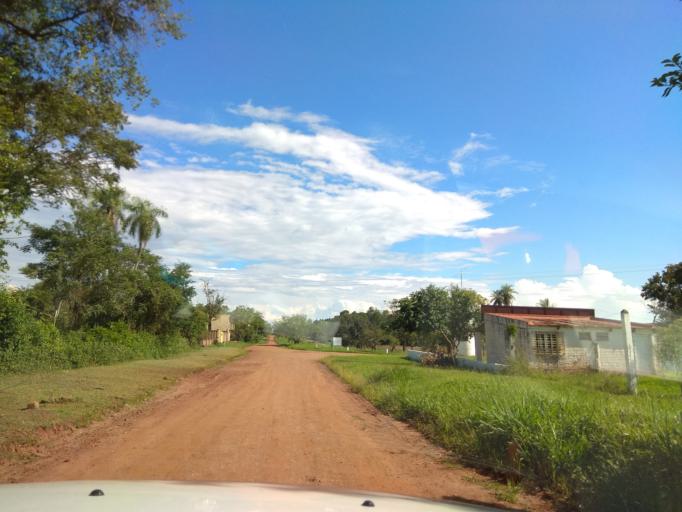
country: AR
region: Misiones
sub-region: Departamento de Candelaria
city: Candelaria
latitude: -27.4548
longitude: -55.7543
